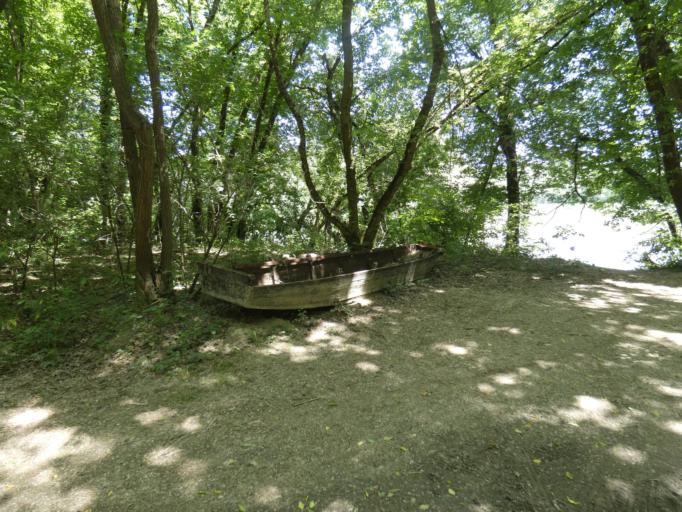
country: HU
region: Tolna
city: Bolcske
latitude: 46.7507
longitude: 18.9731
